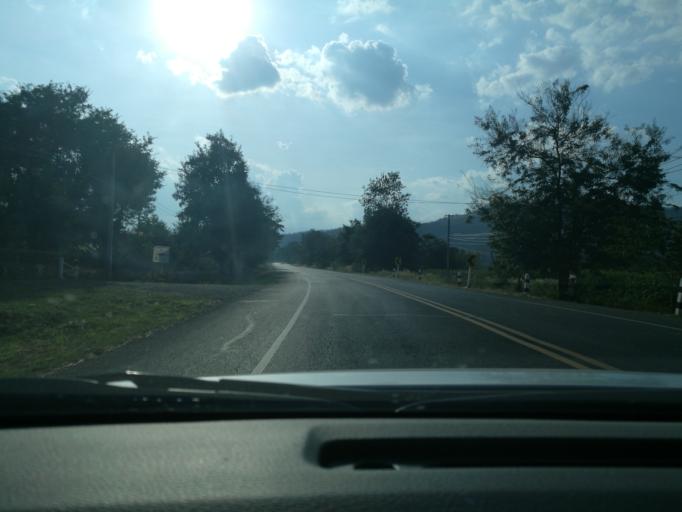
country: TH
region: Phetchabun
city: Phetchabun
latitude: 16.5484
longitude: 101.1255
